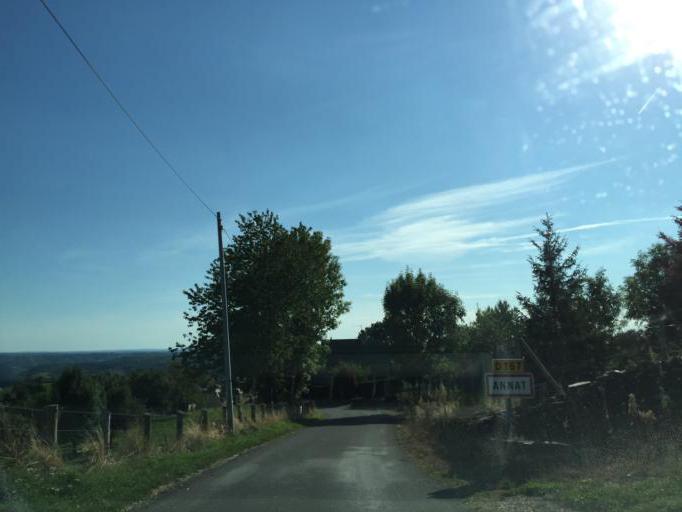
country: FR
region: Midi-Pyrenees
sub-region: Departement de l'Aveyron
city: Espalion
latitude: 44.5748
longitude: 2.6896
